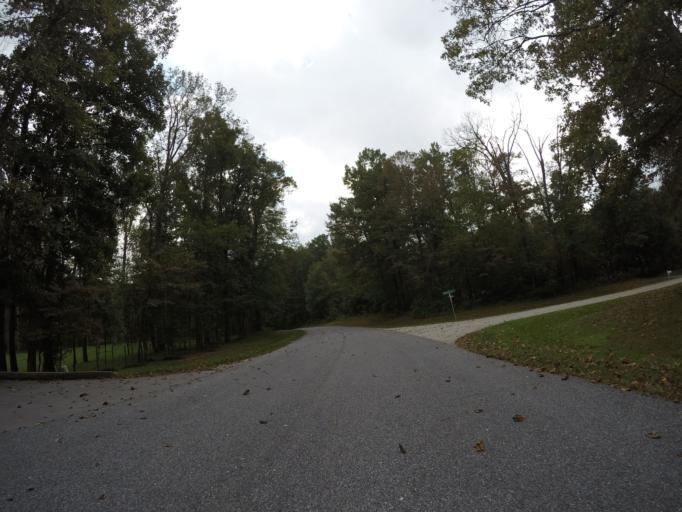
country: US
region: Maryland
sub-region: Howard County
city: Columbia
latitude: 39.2621
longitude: -76.8801
